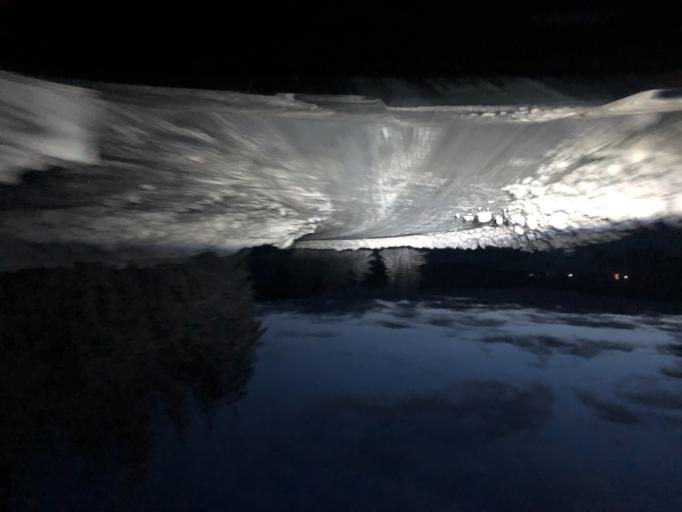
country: SE
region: Vaesternorrland
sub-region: Kramfors Kommun
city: Bollstabruk
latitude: 63.0548
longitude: 17.6690
